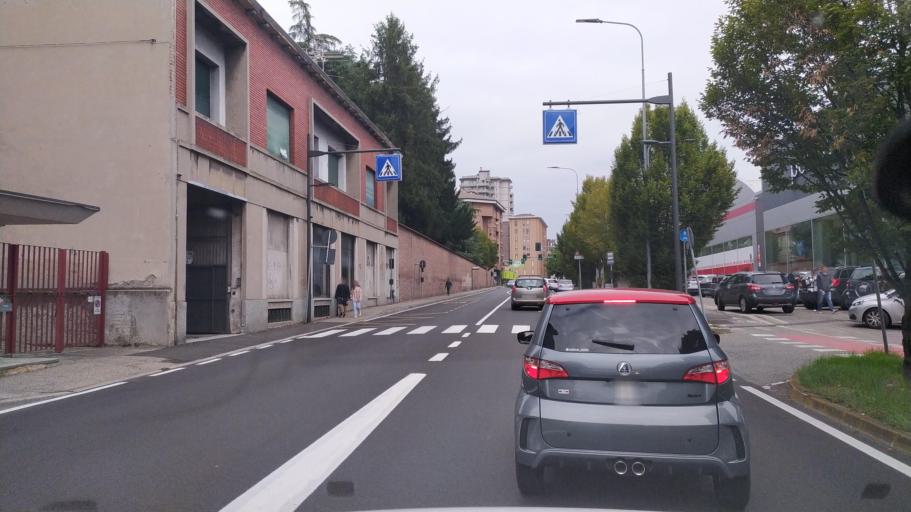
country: IT
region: Lombardy
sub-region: Provincia di Monza e Brianza
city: Seregno
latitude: 45.6455
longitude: 9.2086
